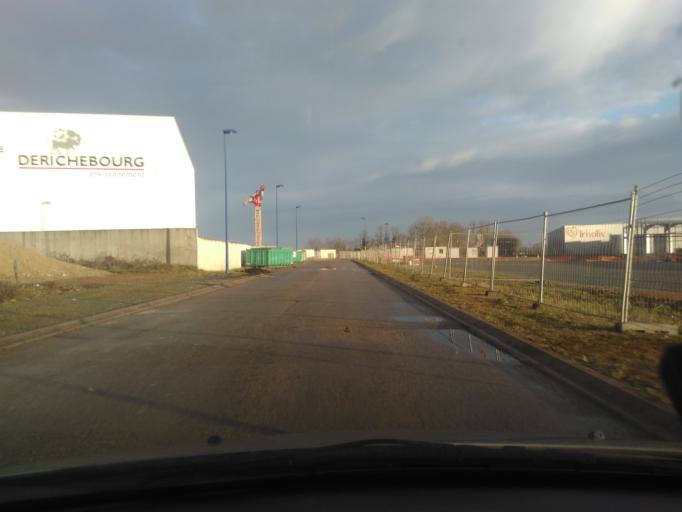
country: FR
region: Pays de la Loire
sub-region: Departement de la Vendee
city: Dompierre-sur-Yon
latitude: 46.6948
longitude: -1.3672
